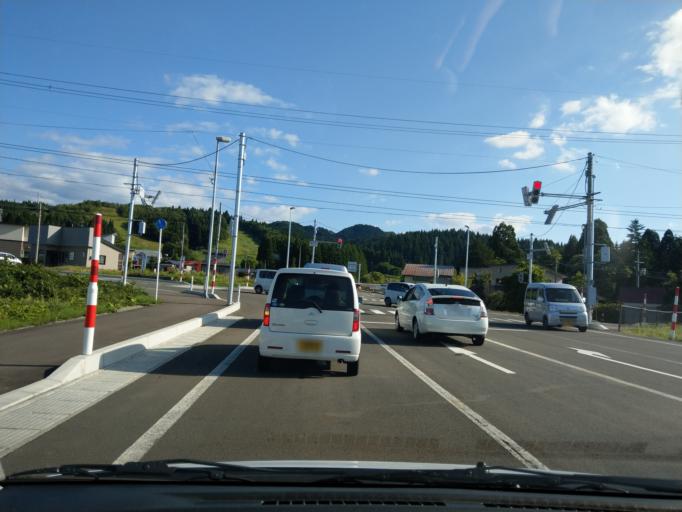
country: JP
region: Akita
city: Takanosu
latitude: 40.1199
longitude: 140.3788
